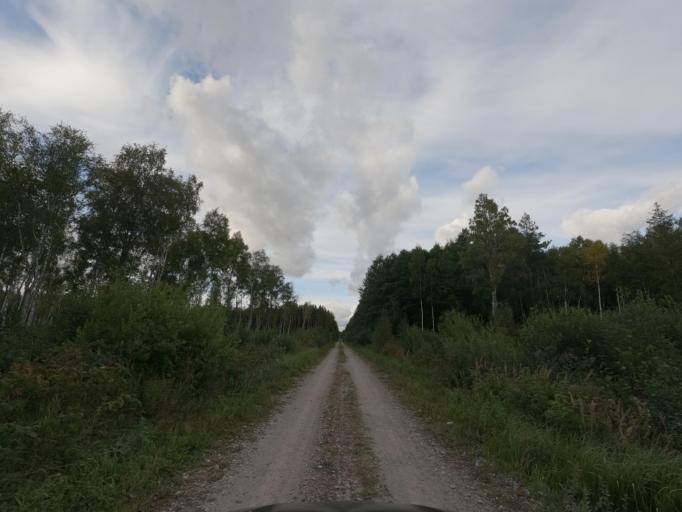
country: EE
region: Raplamaa
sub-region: Rapla vald
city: Rapla
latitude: 59.0058
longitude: 24.7574
